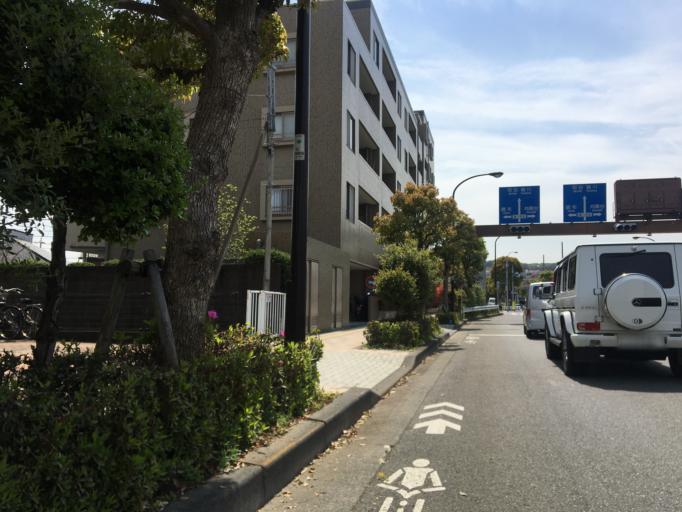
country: JP
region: Tokyo
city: Chofugaoka
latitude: 35.6413
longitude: 139.5089
